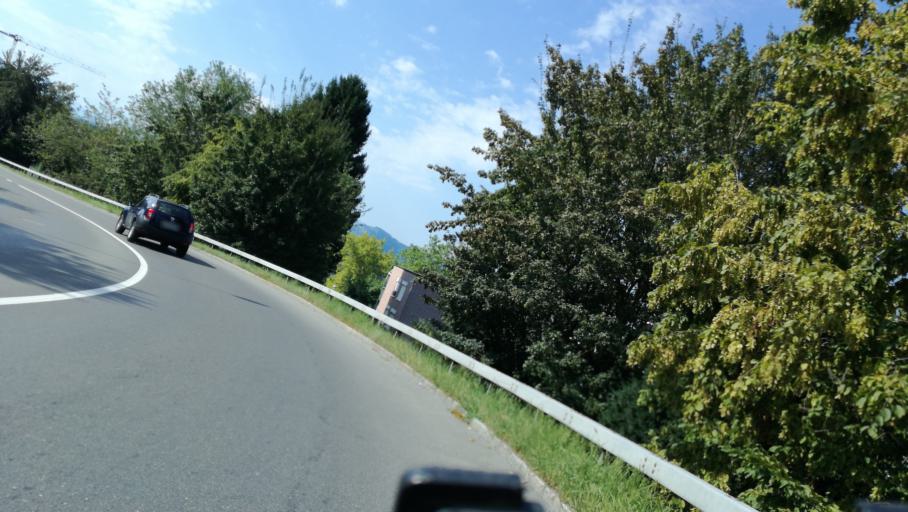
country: CH
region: Zug
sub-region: Zug
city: Zug
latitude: 47.1717
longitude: 8.5261
